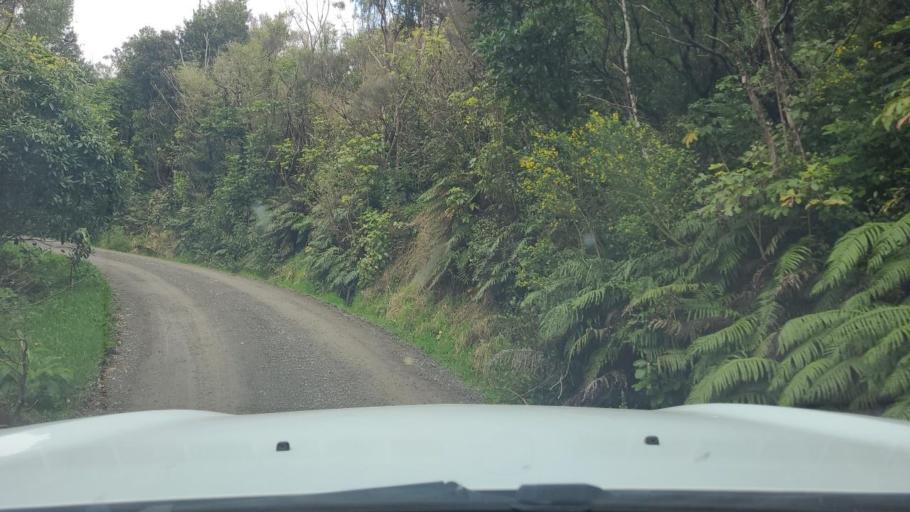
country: NZ
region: Wellington
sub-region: Masterton District
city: Masterton
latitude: -40.9487
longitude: 175.4533
